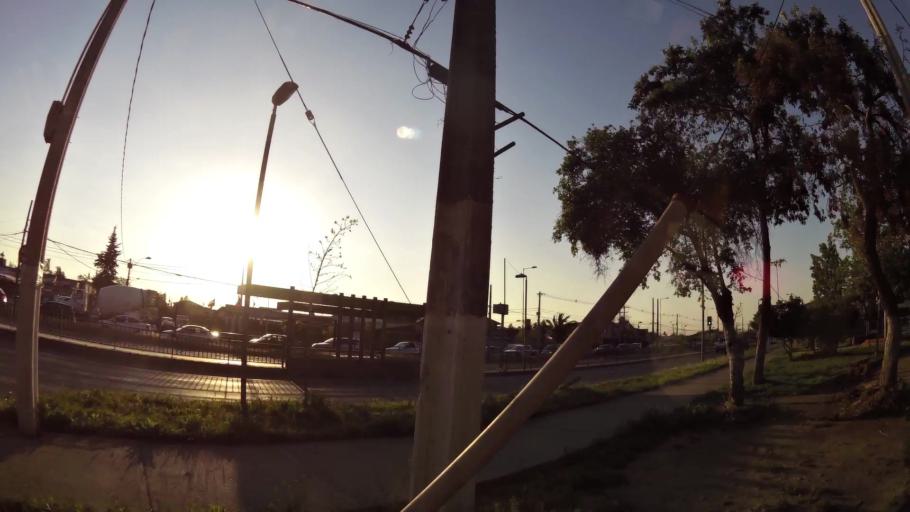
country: CL
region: Santiago Metropolitan
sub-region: Provincia de Santiago
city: La Pintana
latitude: -33.5229
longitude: -70.6228
